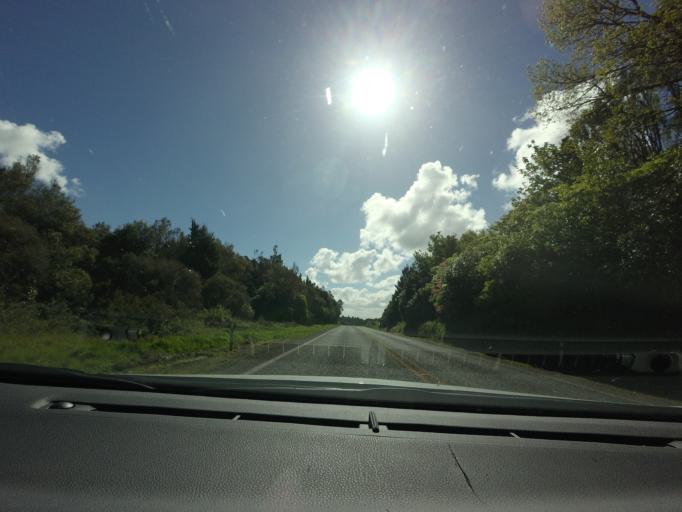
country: NZ
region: Waikato
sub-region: South Waikato District
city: Tokoroa
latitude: -38.0319
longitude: 175.9964
